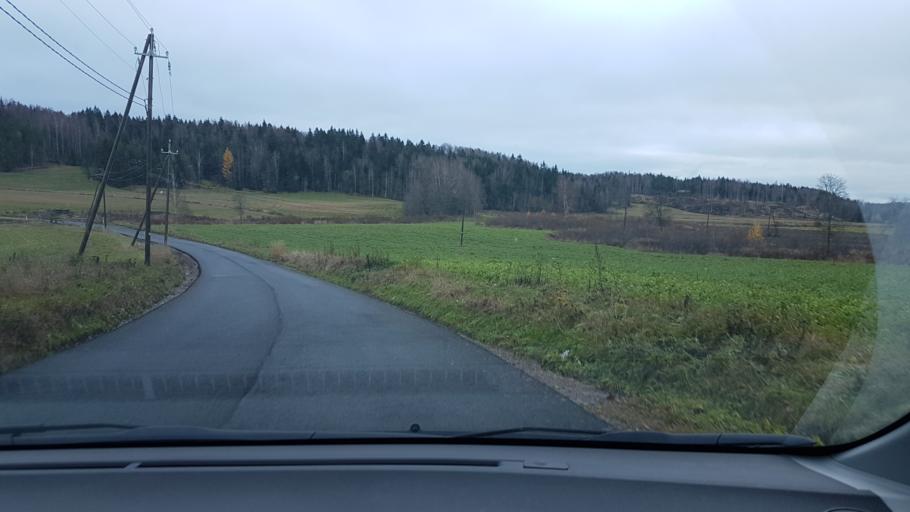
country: FI
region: Uusimaa
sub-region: Helsinki
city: Vantaa
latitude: 60.2829
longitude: 25.1420
